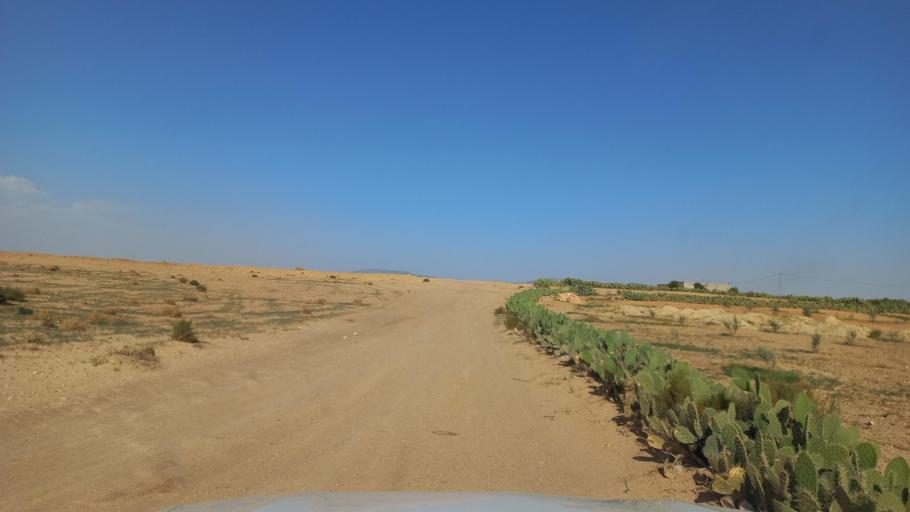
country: TN
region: Al Qasrayn
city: Sbiba
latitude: 35.3215
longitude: 9.0190
